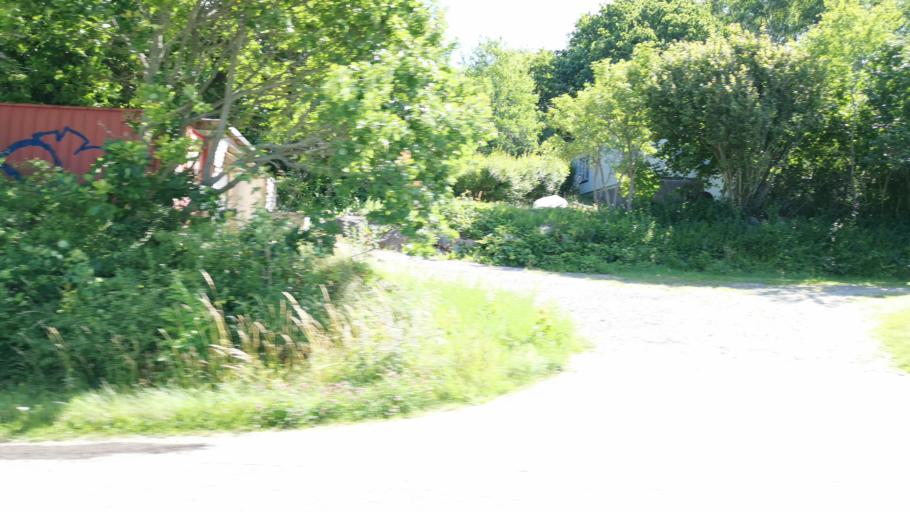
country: SE
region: Vaestra Goetaland
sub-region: Lysekils Kommun
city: Lysekil
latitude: 58.2363
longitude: 11.4570
